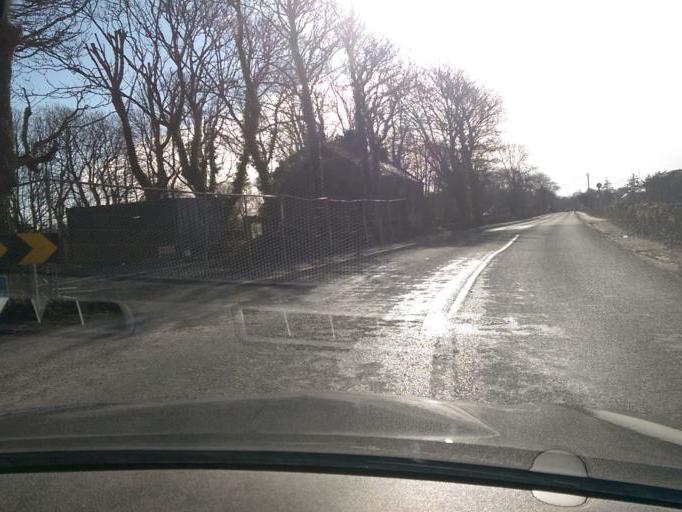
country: IE
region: Connaught
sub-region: County Galway
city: Oranmore
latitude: 53.2521
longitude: -8.9390
